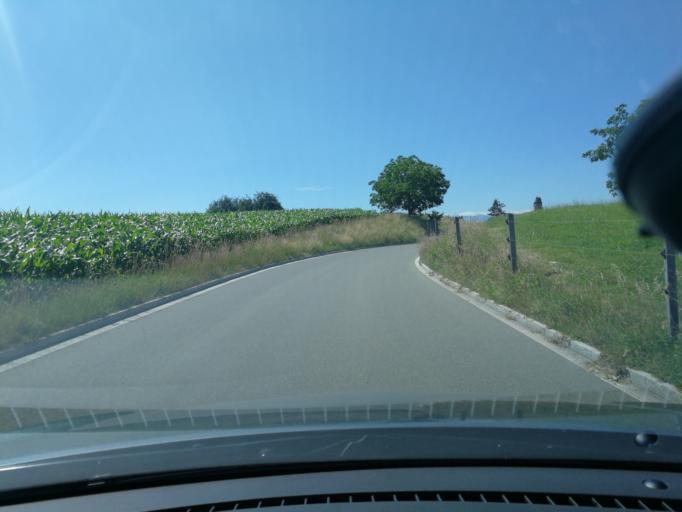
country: CH
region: Zurich
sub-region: Bezirk Meilen
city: Herrliberg
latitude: 47.2968
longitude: 8.6191
